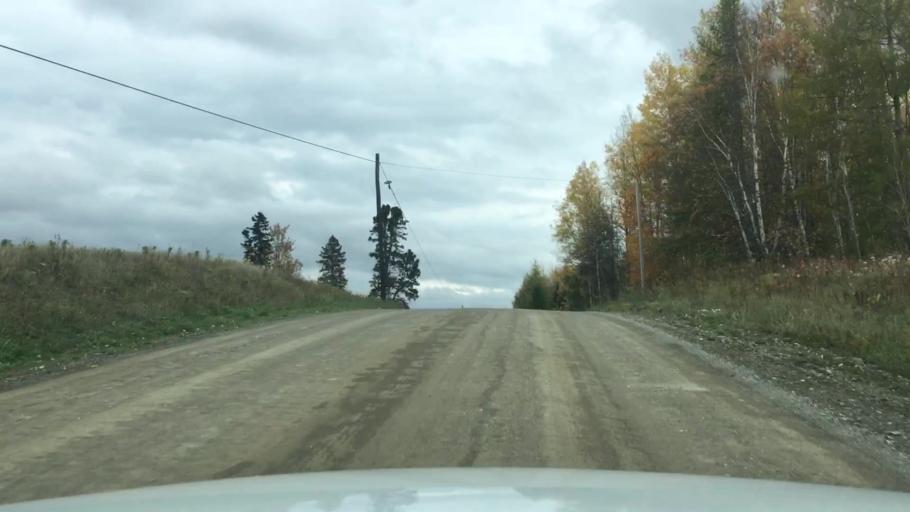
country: US
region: Maine
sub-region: Aroostook County
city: Easton
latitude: 46.5169
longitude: -67.8840
